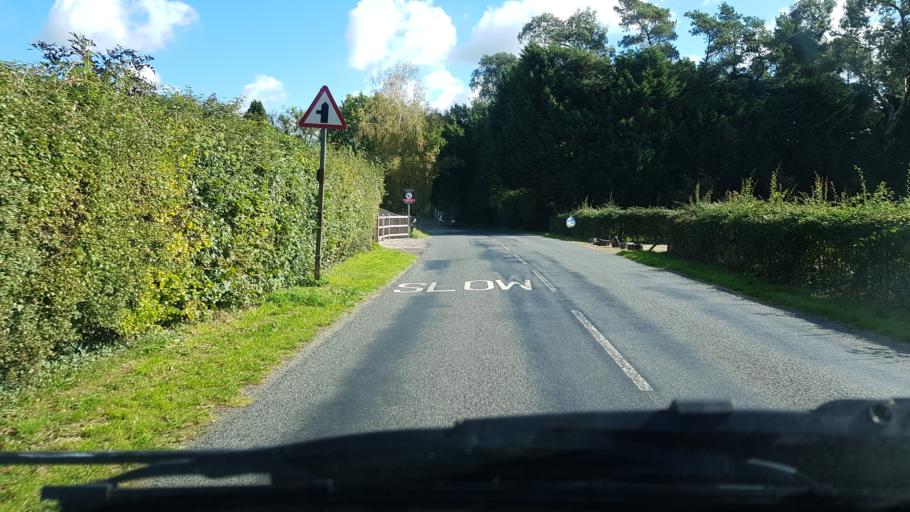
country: GB
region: England
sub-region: West Sussex
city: Rudgwick
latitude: 51.0639
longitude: -0.5324
